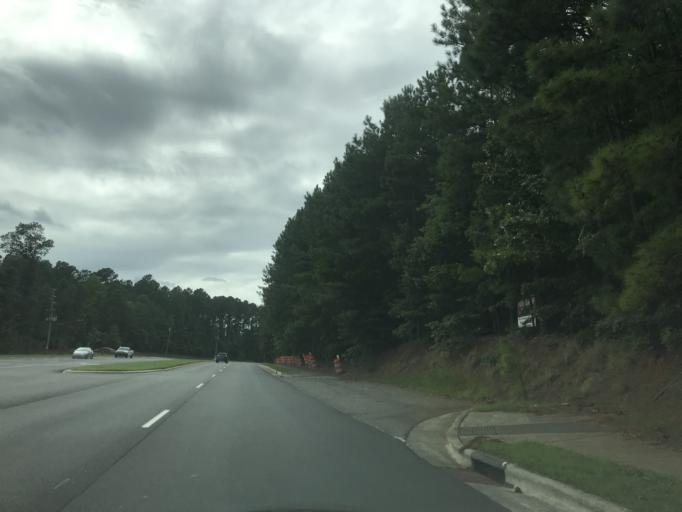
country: US
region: North Carolina
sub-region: Wake County
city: Cary
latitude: 35.7463
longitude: -78.7670
